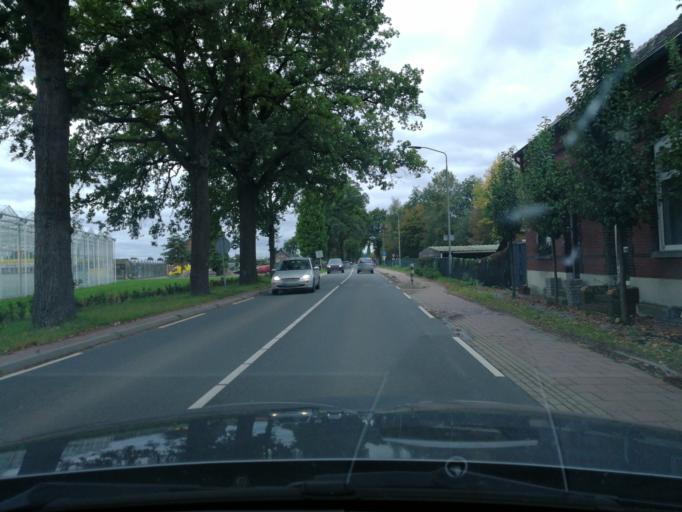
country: NL
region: Limburg
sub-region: Gemeente Venlo
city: Venlo
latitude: 51.3962
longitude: 6.2049
